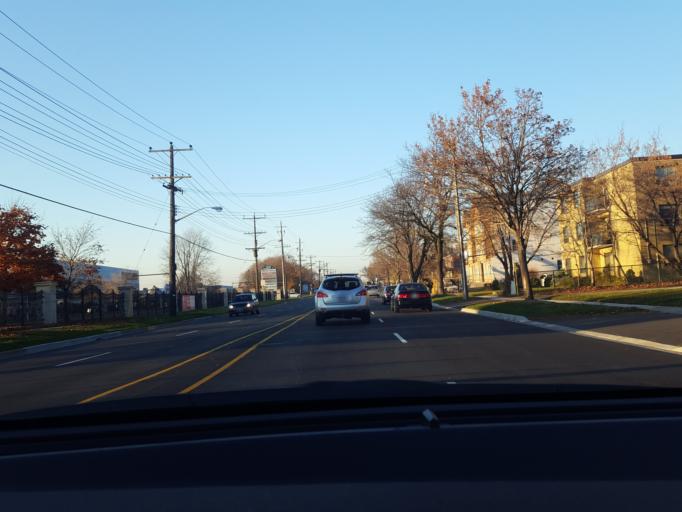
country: CA
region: Ontario
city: Scarborough
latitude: 43.7563
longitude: -79.2885
